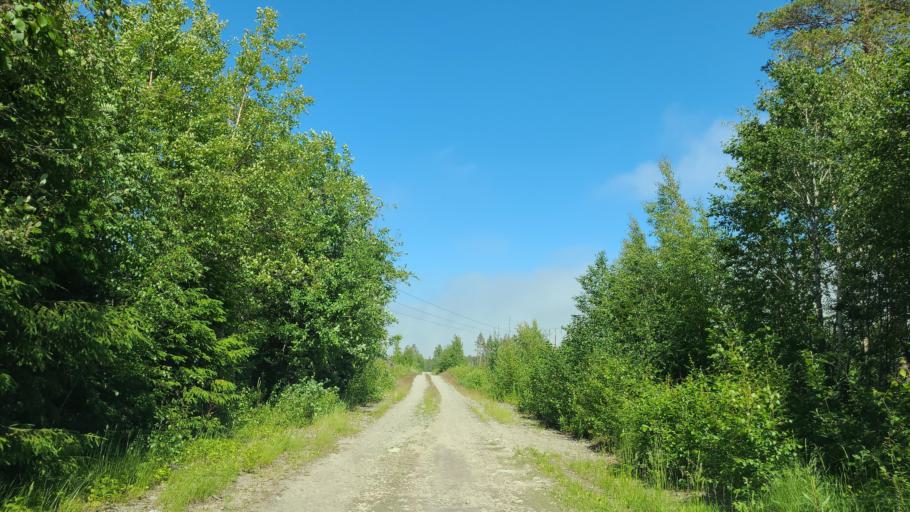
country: SE
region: Vaesternorrland
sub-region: OErnskoeldsviks Kommun
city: Husum
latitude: 63.4403
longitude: 19.2336
